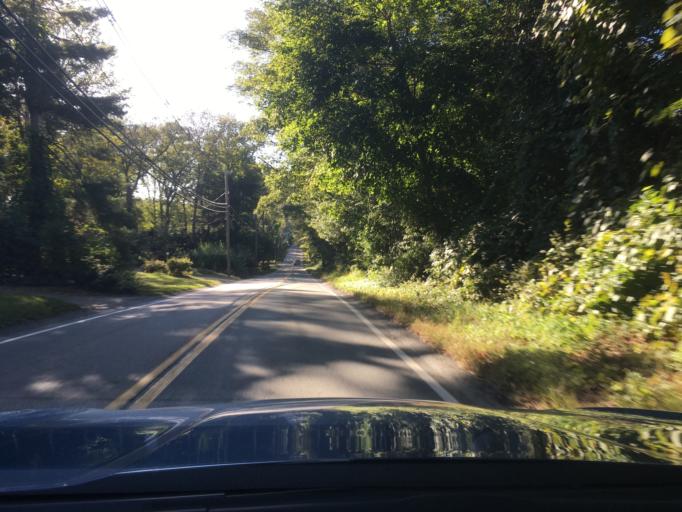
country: US
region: Rhode Island
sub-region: Kent County
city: East Greenwich
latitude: 41.6637
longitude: -71.4607
